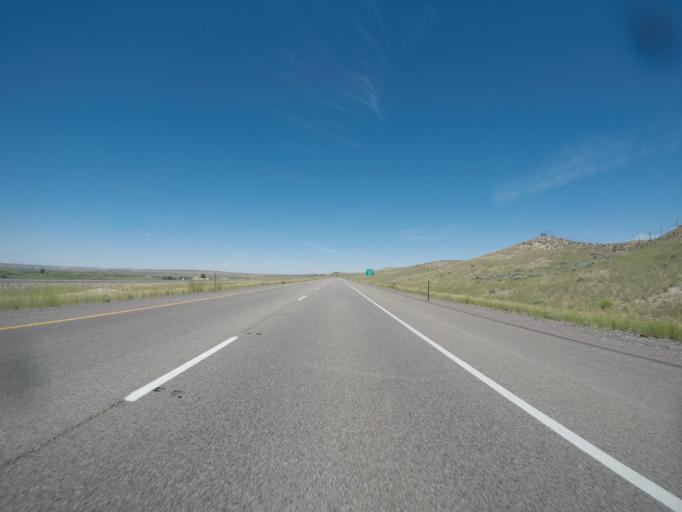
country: US
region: Wyoming
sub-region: Carbon County
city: Saratoga
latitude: 41.7416
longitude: -106.7629
